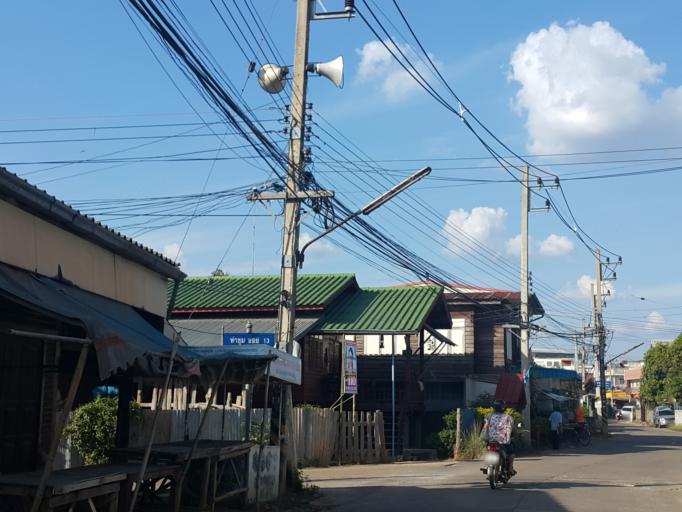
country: TH
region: Sukhothai
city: Thung Saliam
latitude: 17.3153
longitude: 99.5530
